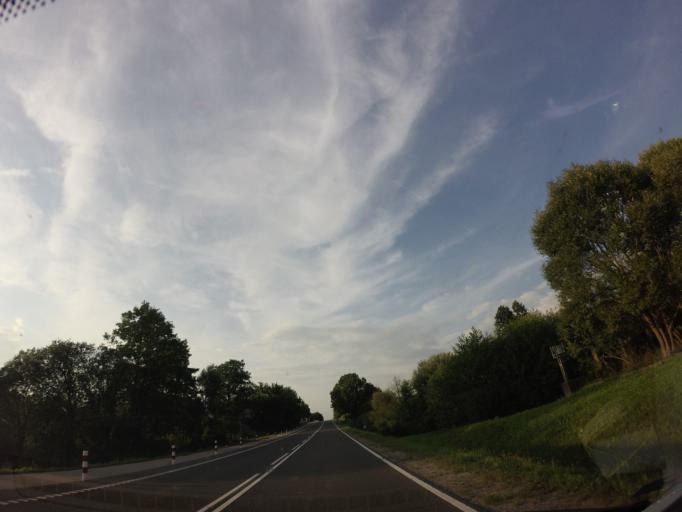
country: LT
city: Lazdijai
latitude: 54.1505
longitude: 23.4699
